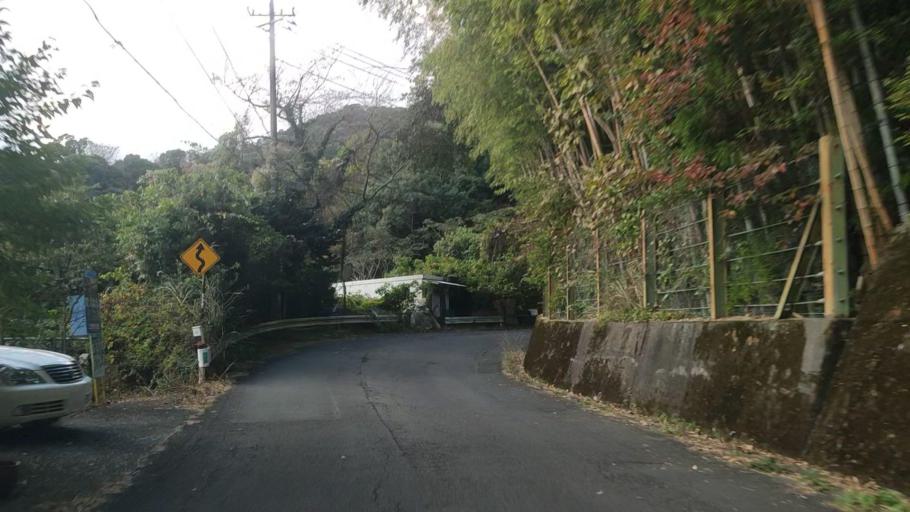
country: JP
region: Shizuoka
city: Ito
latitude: 34.9553
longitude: 139.0754
